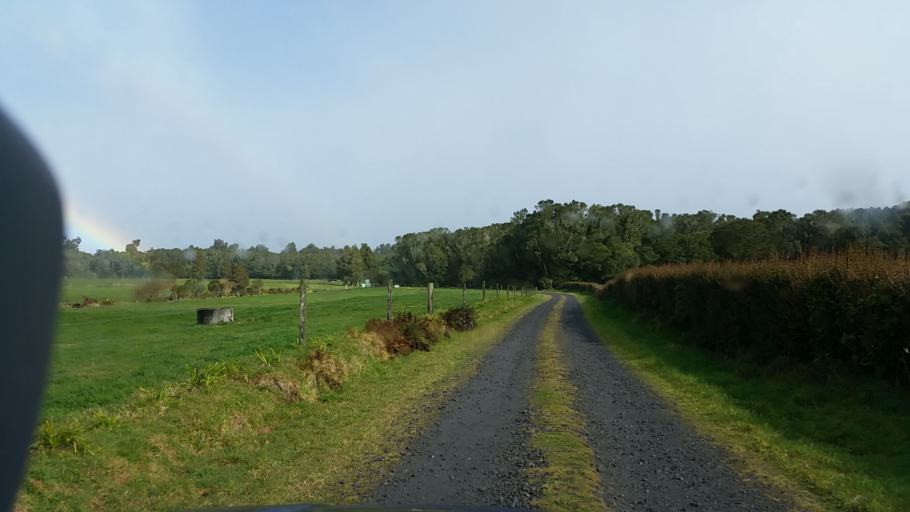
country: NZ
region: Taranaki
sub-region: South Taranaki District
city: Eltham
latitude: -39.2869
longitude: 174.1798
